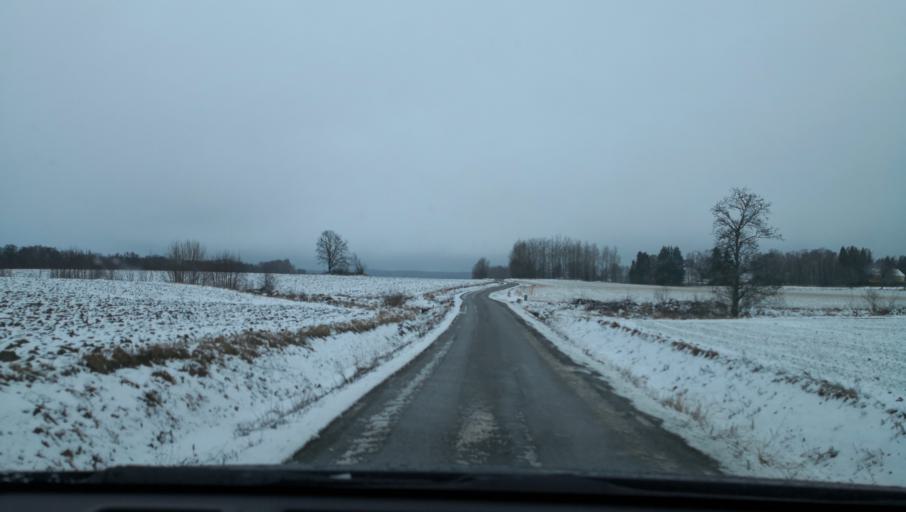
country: SE
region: Vaestmanland
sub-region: Kopings Kommun
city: Kolsva
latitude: 59.5389
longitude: 15.8818
